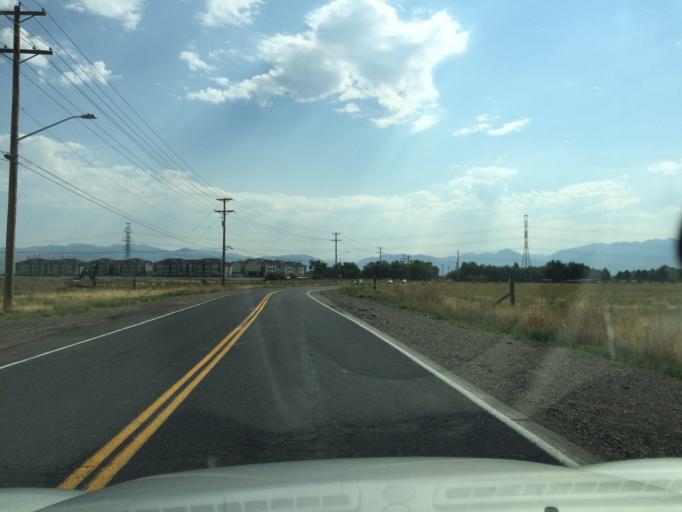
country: US
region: Utah
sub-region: Salt Lake County
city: West Valley City
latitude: 40.7106
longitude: -112.0345
